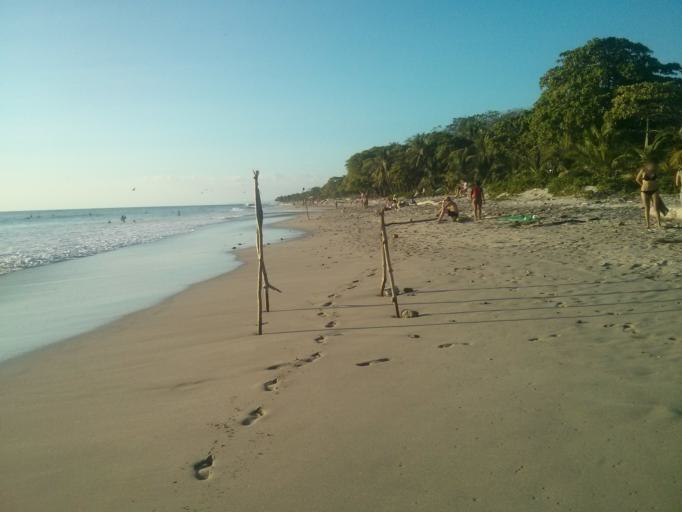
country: CR
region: Guanacaste
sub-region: Canton de Nandayure
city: Bejuco
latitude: 9.6273
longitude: -85.1530
